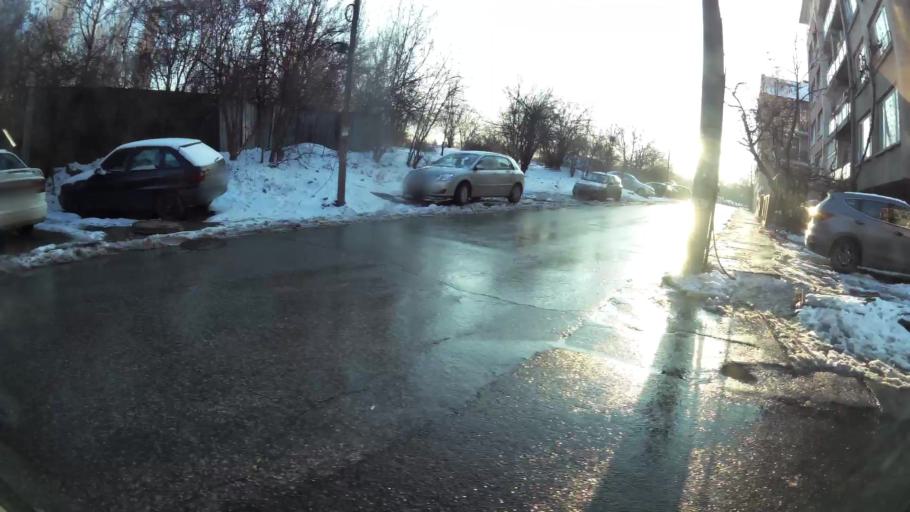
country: BG
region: Sofia-Capital
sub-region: Stolichna Obshtina
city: Sofia
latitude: 42.6880
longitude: 23.3665
